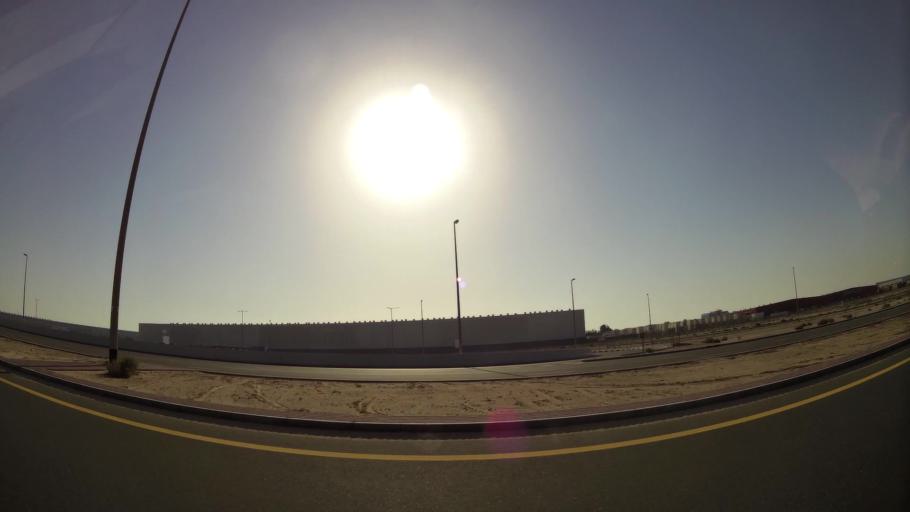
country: AE
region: Dubai
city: Dubai
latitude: 24.9741
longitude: 55.1123
